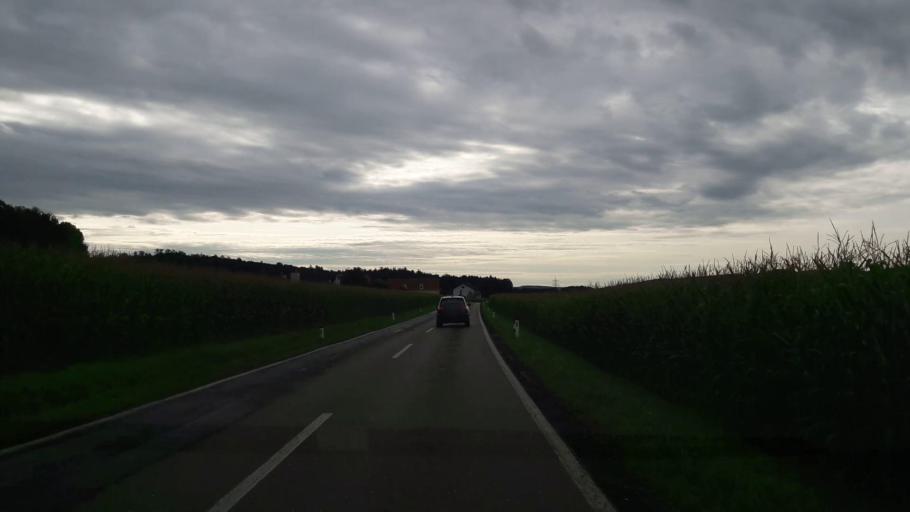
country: AT
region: Styria
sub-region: Politischer Bezirk Hartberg-Fuerstenfeld
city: Ebersdorf
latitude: 47.2141
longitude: 15.9285
